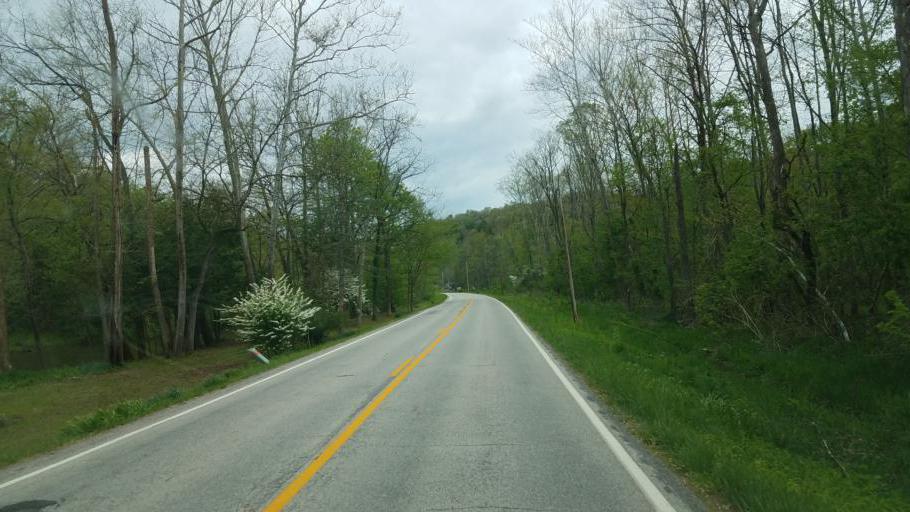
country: US
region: Ohio
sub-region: Ashland County
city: Loudonville
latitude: 40.5958
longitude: -82.2241
